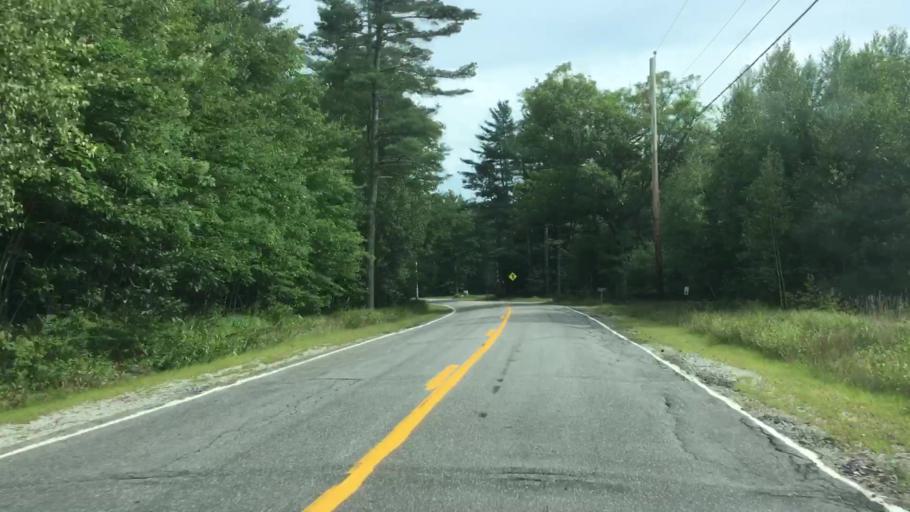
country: US
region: Maine
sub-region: Oxford County
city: Bethel
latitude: 44.3335
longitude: -70.7771
